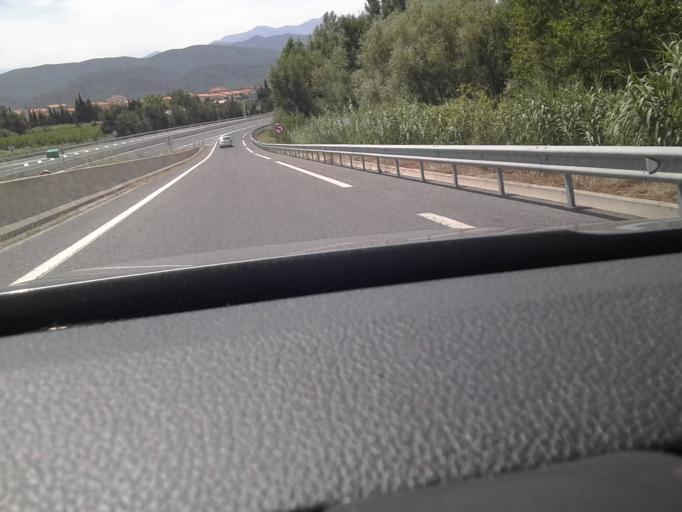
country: FR
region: Languedoc-Roussillon
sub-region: Departement des Pyrenees-Orientales
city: Ille-sur-Tet
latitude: 42.6803
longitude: 2.6292
